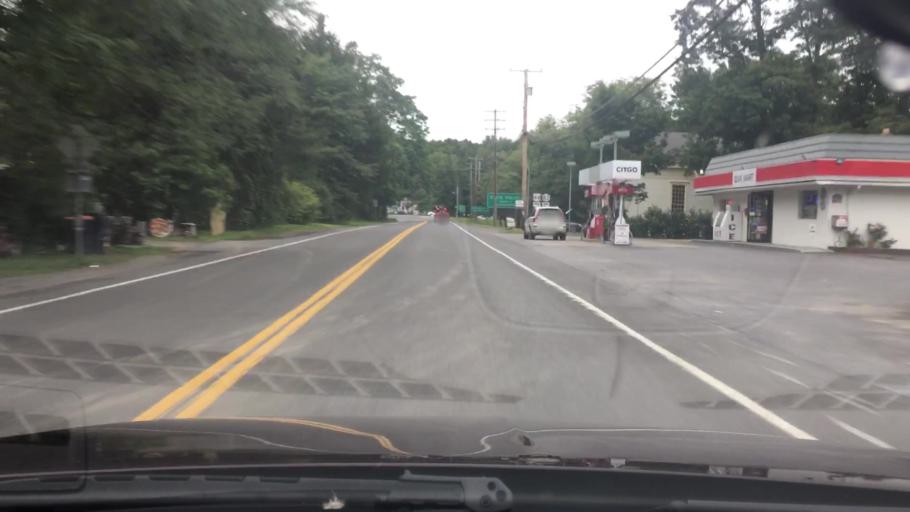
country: US
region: New York
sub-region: Dutchess County
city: Millbrook
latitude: 41.7817
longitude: -73.7534
